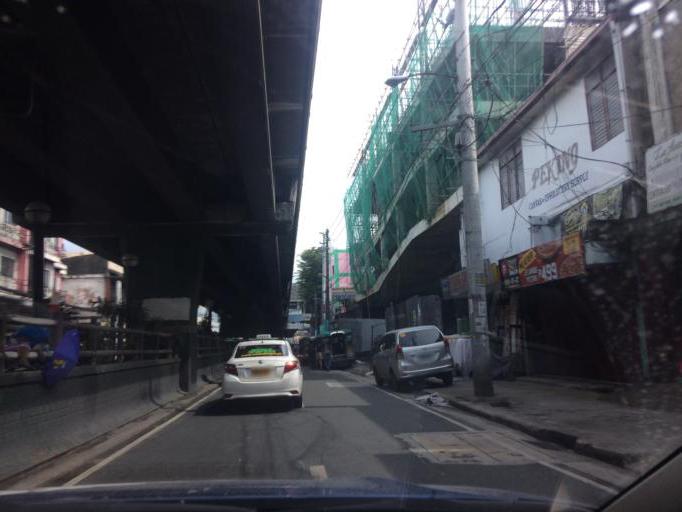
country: PH
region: Metro Manila
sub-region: Makati City
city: Makati City
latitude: 14.5493
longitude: 120.9982
